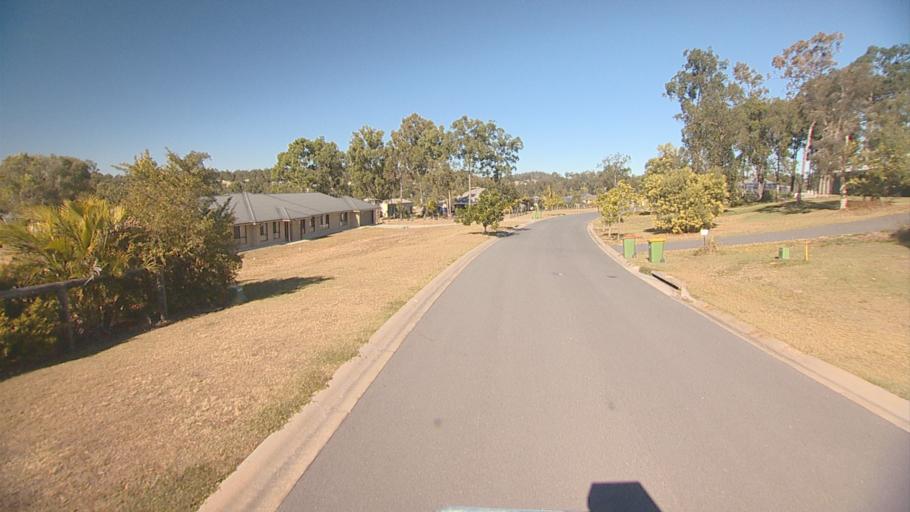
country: AU
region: Queensland
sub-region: Logan
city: North Maclean
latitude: -27.7516
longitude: 152.9501
